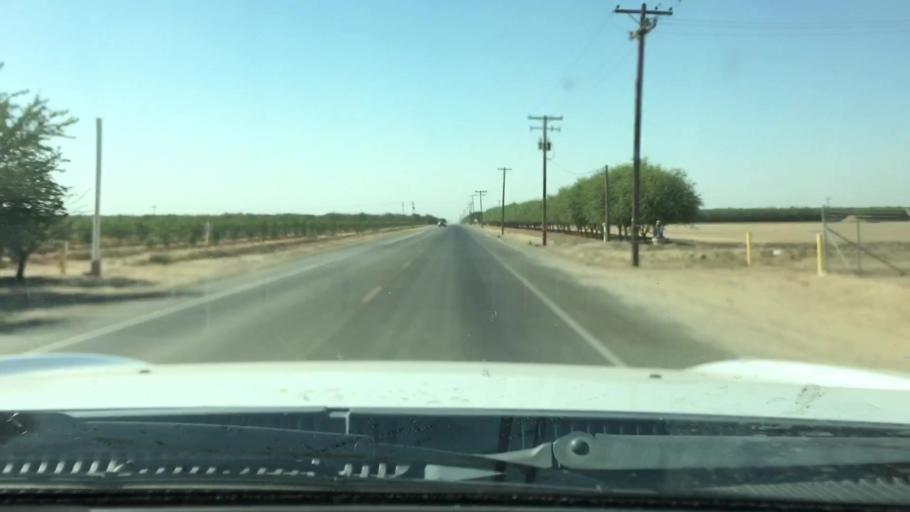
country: US
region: California
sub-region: Kern County
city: Wasco
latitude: 35.5635
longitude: -119.4742
